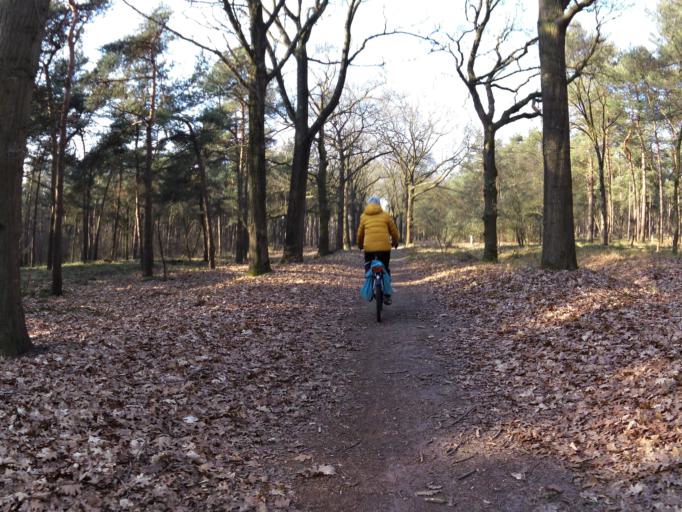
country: NL
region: North Brabant
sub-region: Gemeente Maasdonk
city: Geffen
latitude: 51.7159
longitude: 5.4142
